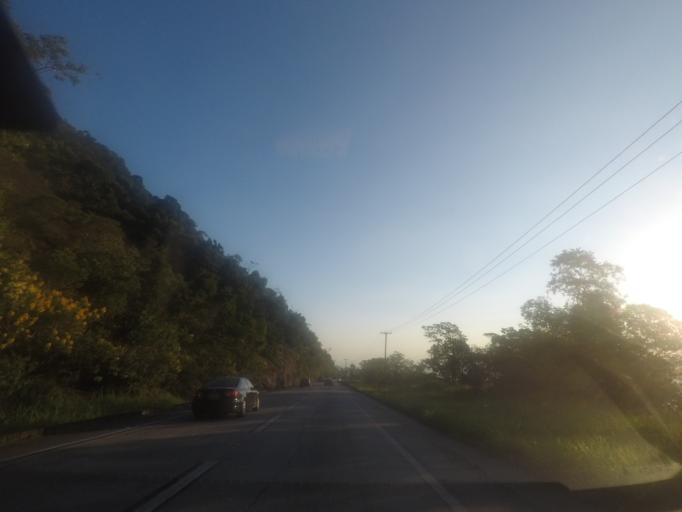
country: BR
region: Rio de Janeiro
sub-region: Petropolis
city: Petropolis
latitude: -22.5270
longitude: -43.2345
